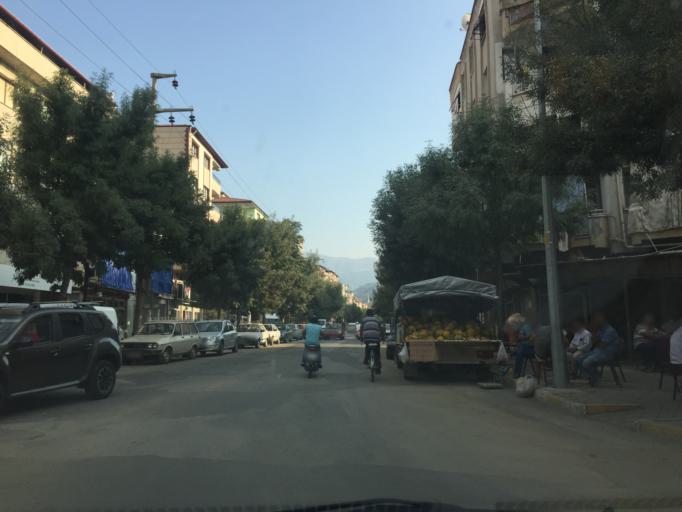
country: TR
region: Manisa
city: Salihli
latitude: 38.4880
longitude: 28.1512
